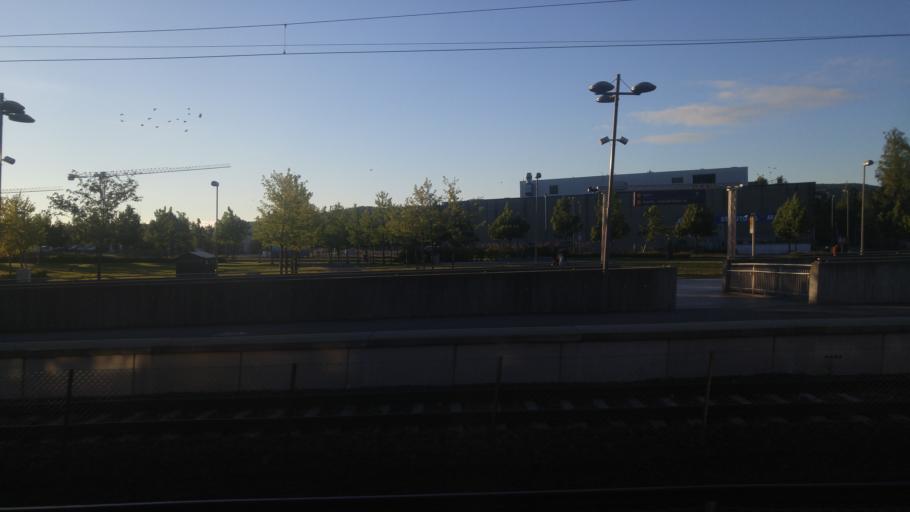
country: NO
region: Akershus
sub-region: Skedsmo
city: Lillestrom
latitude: 59.9498
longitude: 11.0023
